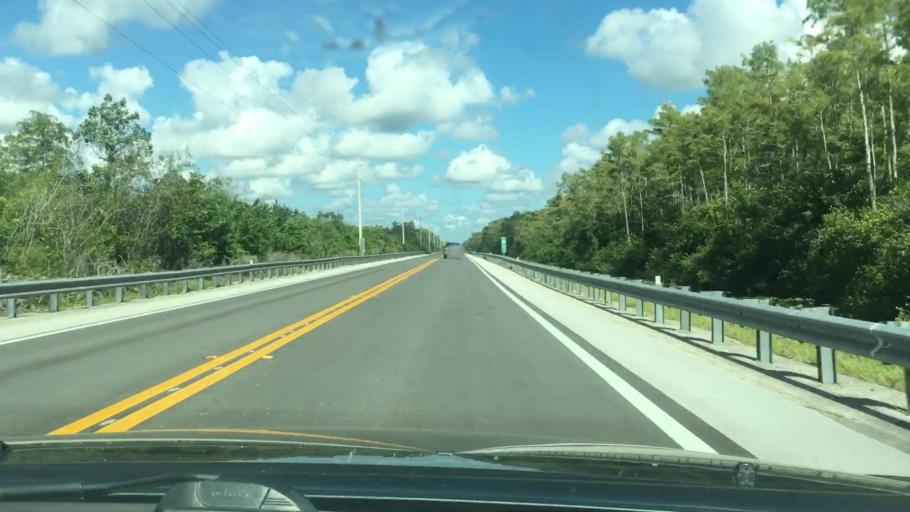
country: US
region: Florida
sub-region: Miami-Dade County
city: Kendall West
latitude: 25.7647
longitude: -80.8312
